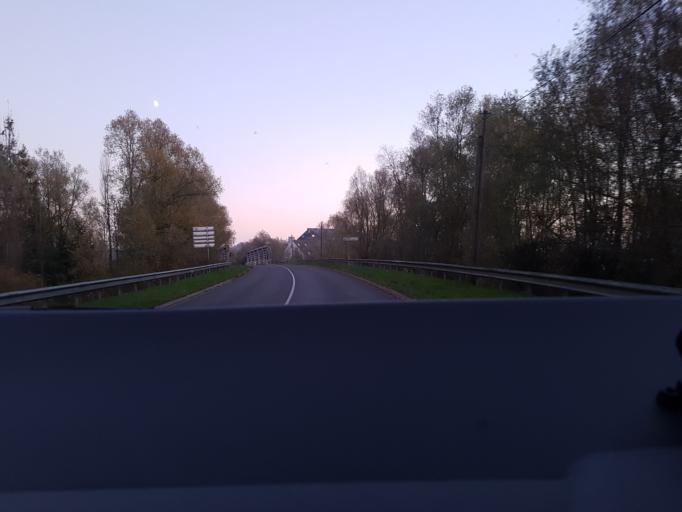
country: FR
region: Nord-Pas-de-Calais
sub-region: Departement du Nord
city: Watten
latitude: 50.8399
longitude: 2.2074
